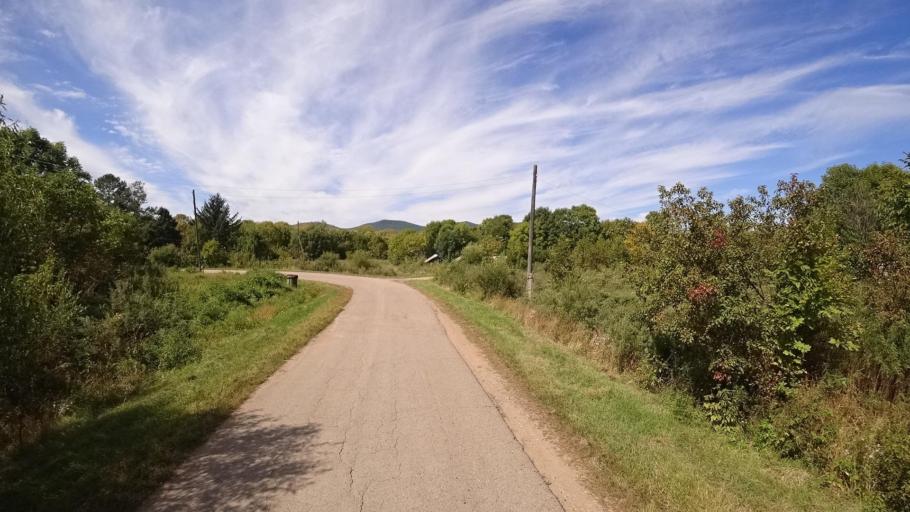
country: RU
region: Primorskiy
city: Kirovskiy
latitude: 44.7593
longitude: 133.6081
